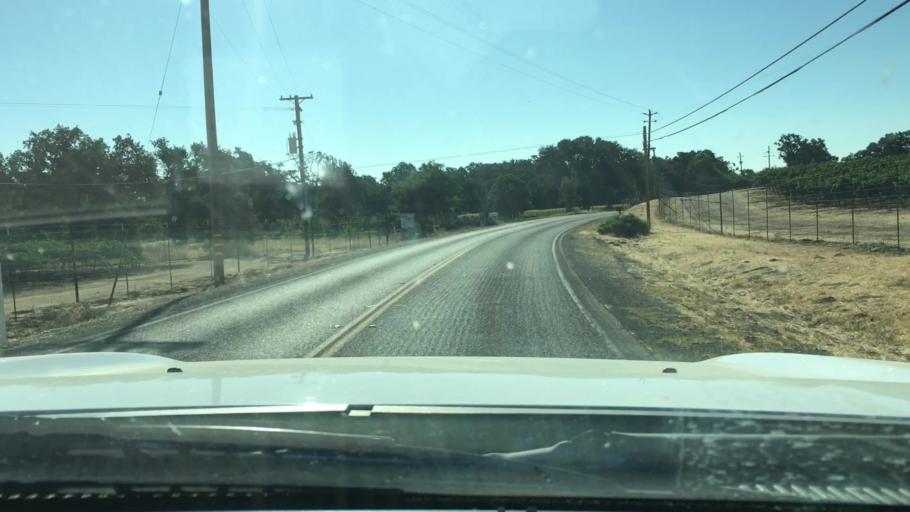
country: US
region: California
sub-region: San Luis Obispo County
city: Paso Robles
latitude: 35.5752
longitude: -120.6115
